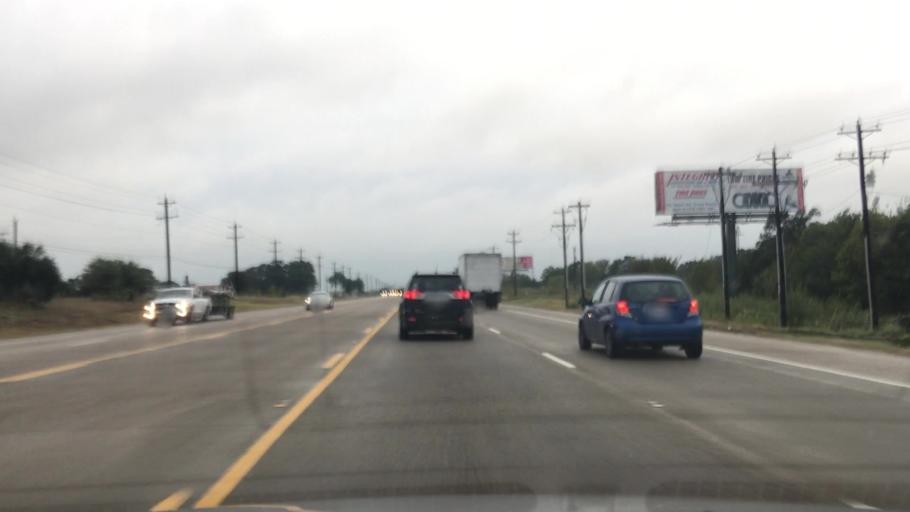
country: US
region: Texas
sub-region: Denton County
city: Oak Point
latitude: 33.2216
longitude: -96.9515
